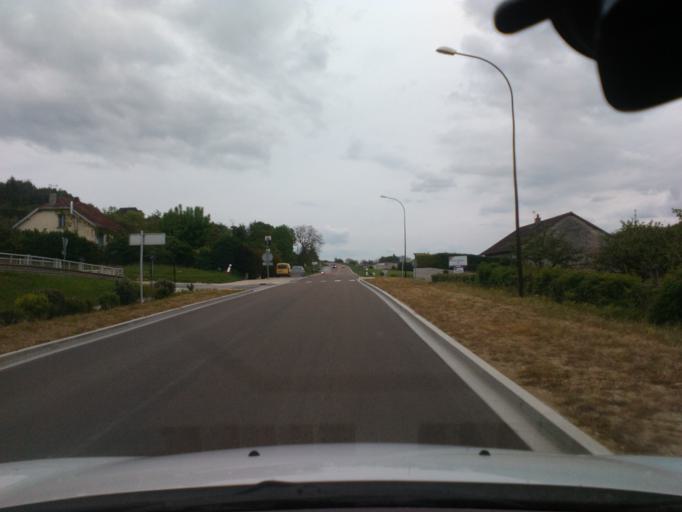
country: FR
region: Champagne-Ardenne
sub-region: Departement de l'Aube
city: Bar-sur-Aube
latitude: 48.2665
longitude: 4.6533
